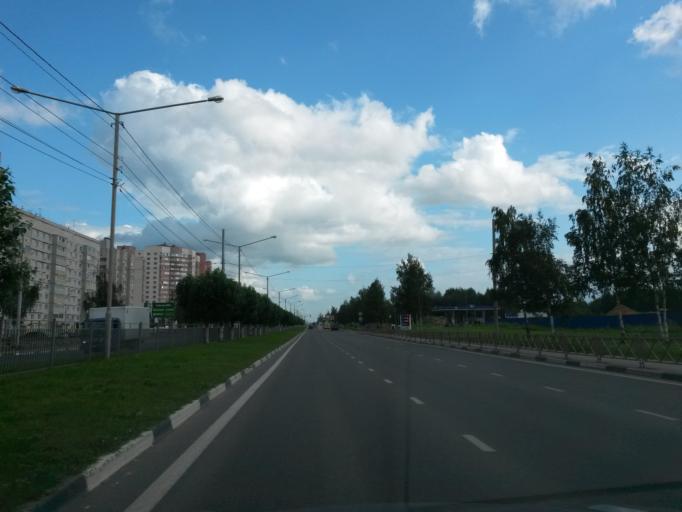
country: RU
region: Jaroslavl
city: Yaroslavl
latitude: 57.5861
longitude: 39.9052
